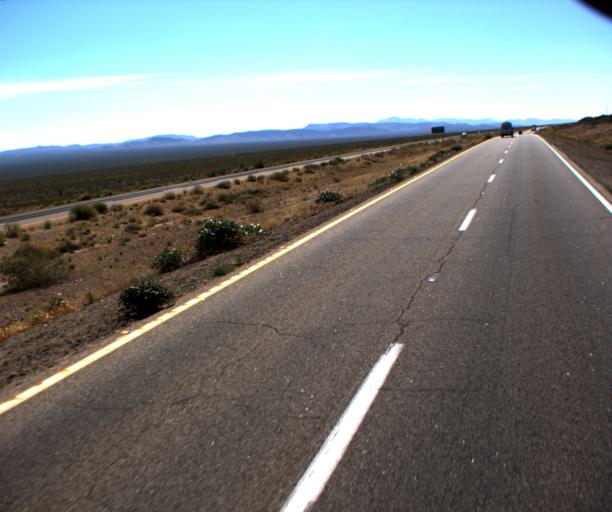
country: US
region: Arizona
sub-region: Mohave County
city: Dolan Springs
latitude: 35.7884
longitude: -114.5245
